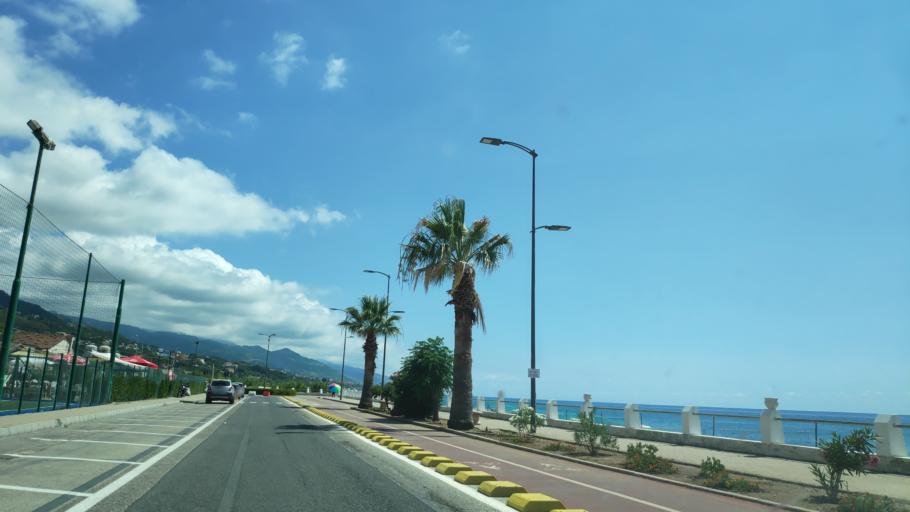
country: IT
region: Calabria
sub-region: Provincia di Cosenza
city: Paola
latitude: 39.3547
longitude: 16.0338
